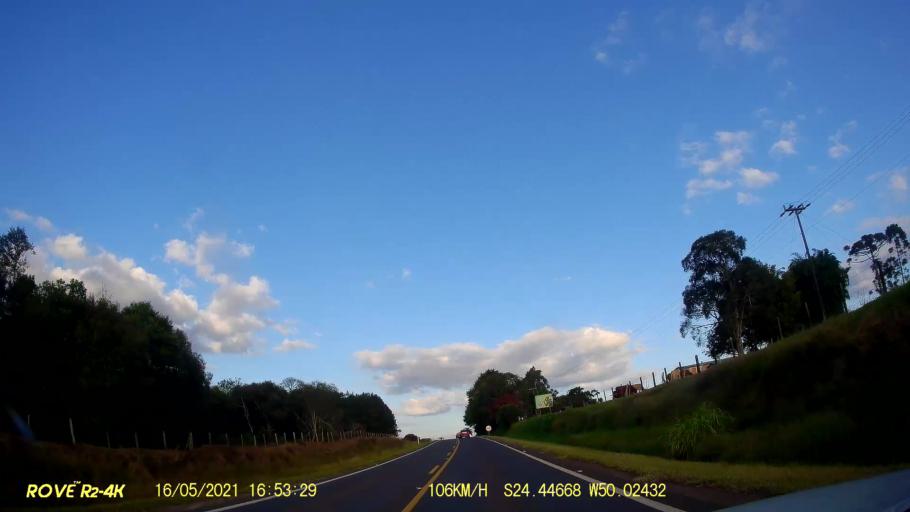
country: BR
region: Parana
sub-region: Pirai Do Sul
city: Pirai do Sul
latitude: -24.4467
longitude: -50.0240
